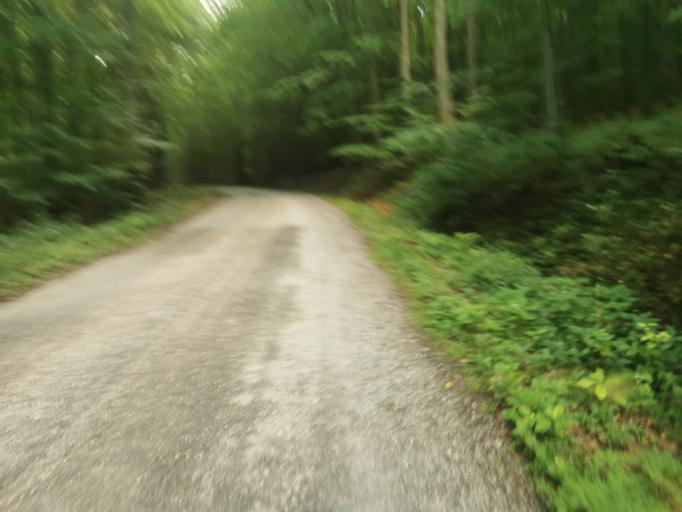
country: SK
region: Trenciansky
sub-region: Okres Myjava
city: Myjava
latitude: 48.7912
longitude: 17.6077
